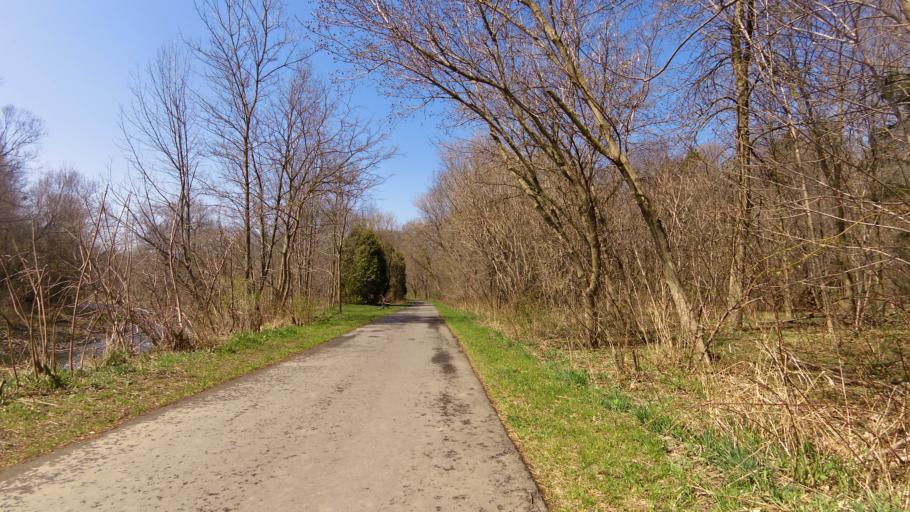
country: CA
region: Ontario
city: Etobicoke
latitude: 43.5986
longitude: -79.5535
